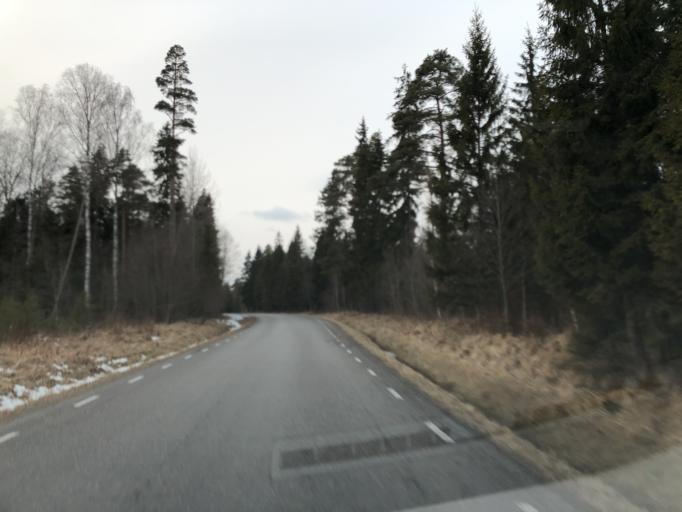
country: EE
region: Paernumaa
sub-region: Vaendra vald (alev)
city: Vandra
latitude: 58.6926
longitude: 24.9765
